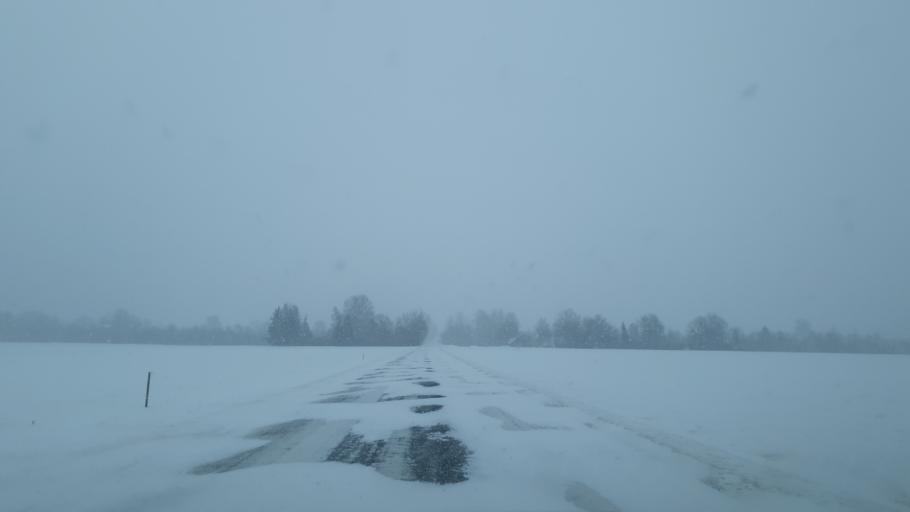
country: EE
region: Jogevamaa
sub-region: Jogeva linn
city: Jogeva
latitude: 58.8233
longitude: 26.3690
